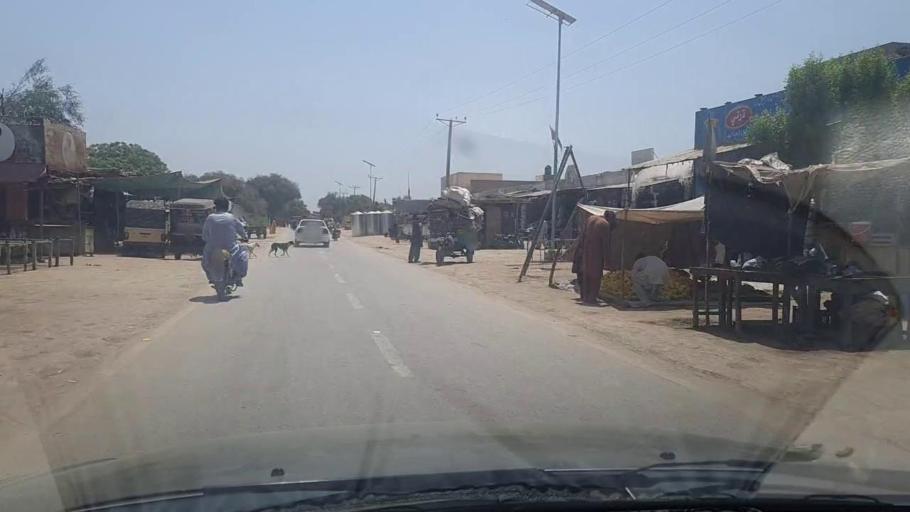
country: PK
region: Sindh
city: Tando Jam
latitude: 25.3087
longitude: 68.5752
